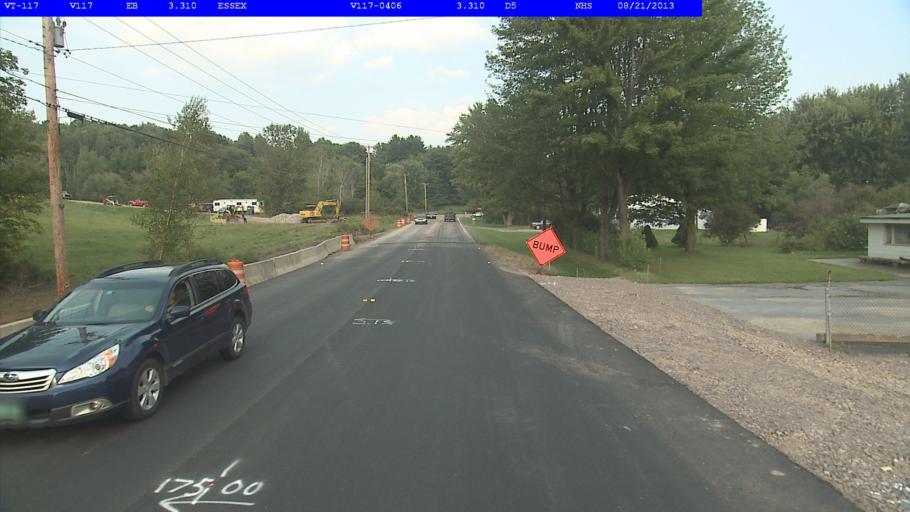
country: US
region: Vermont
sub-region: Chittenden County
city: Williston
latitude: 44.4790
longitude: -73.0487
